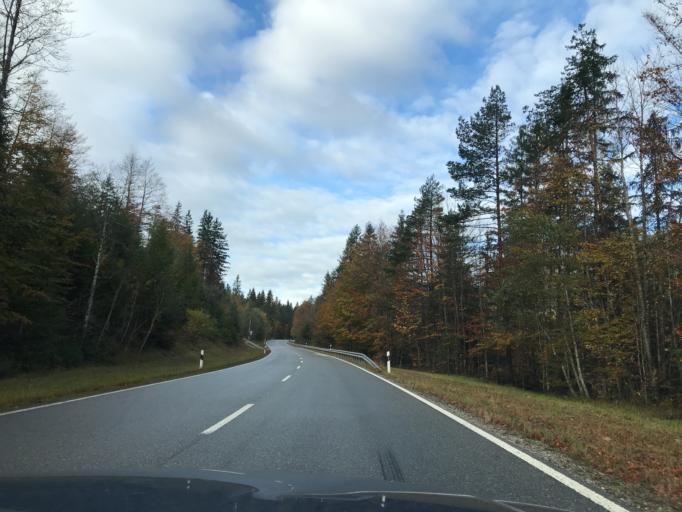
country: DE
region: Bavaria
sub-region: Upper Bavaria
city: Jachenau
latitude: 47.5586
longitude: 11.4802
